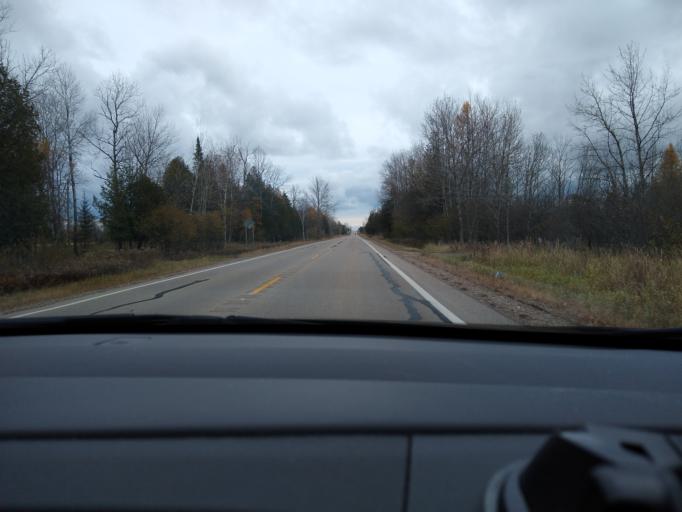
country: US
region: Michigan
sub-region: Delta County
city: Escanaba
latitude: 45.7864
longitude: -87.3348
